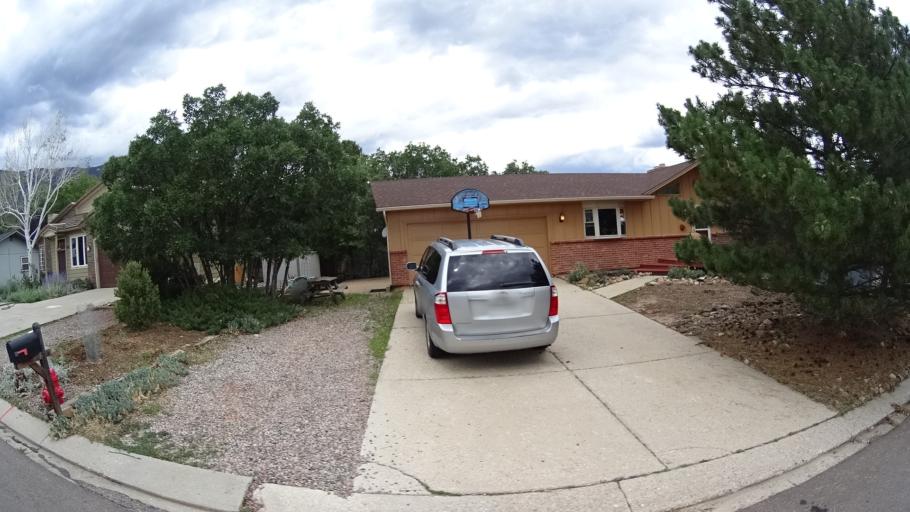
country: US
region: Colorado
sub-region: El Paso County
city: Manitou Springs
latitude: 38.8440
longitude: -104.8956
